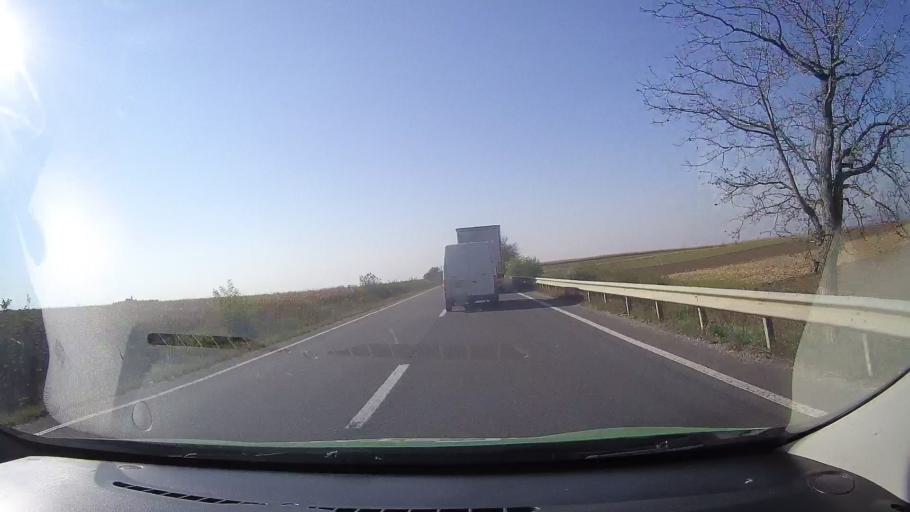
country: RO
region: Satu Mare
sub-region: Comuna Petresti
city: Petresti
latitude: 47.6340
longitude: 22.3972
